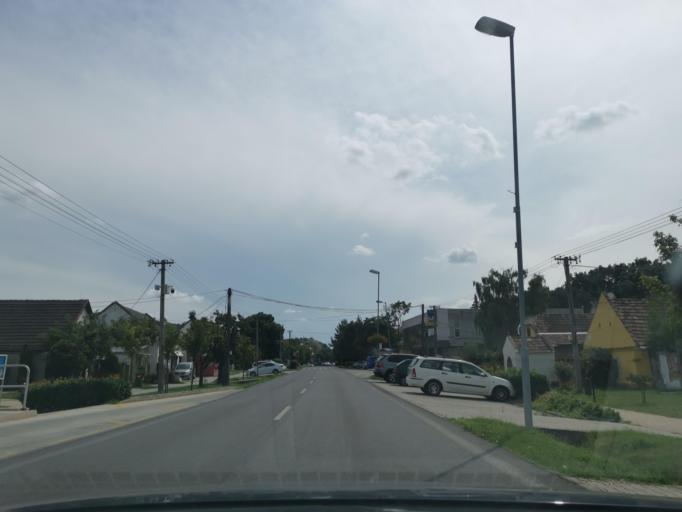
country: AT
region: Lower Austria
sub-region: Politischer Bezirk Bruck an der Leitha
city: Hainburg an der Donau
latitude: 48.2123
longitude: 16.9734
